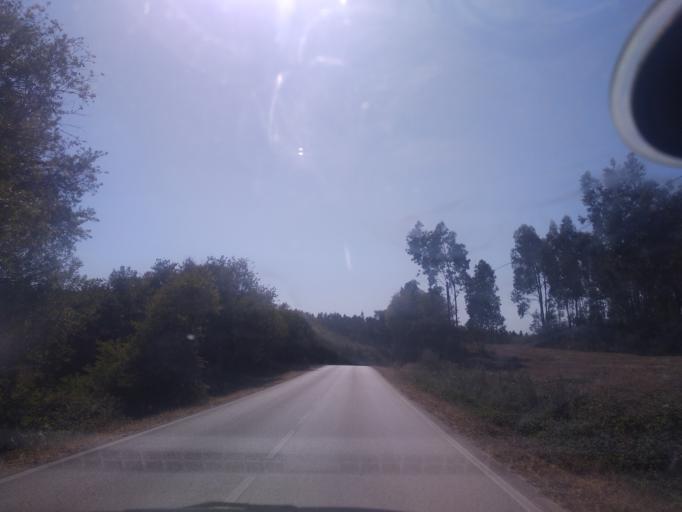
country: PT
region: Faro
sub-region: Aljezur
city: Aljezur
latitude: 37.2203
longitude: -8.7996
